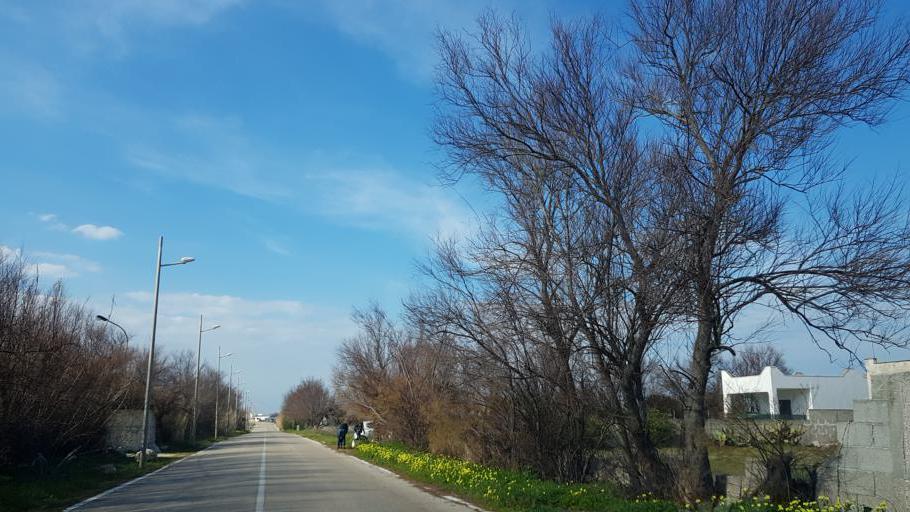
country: IT
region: Apulia
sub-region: Provincia di Brindisi
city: Brindisi
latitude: 40.6912
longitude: 17.8371
